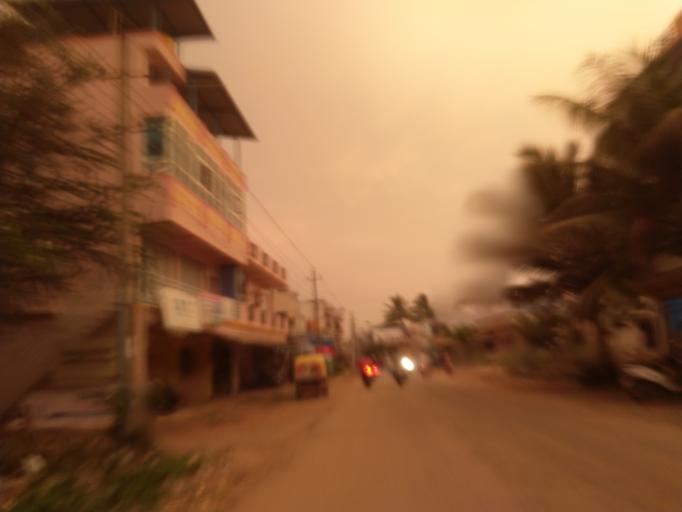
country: IN
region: Karnataka
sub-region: Hassan
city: Hassan
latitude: 13.0169
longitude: 76.1125
